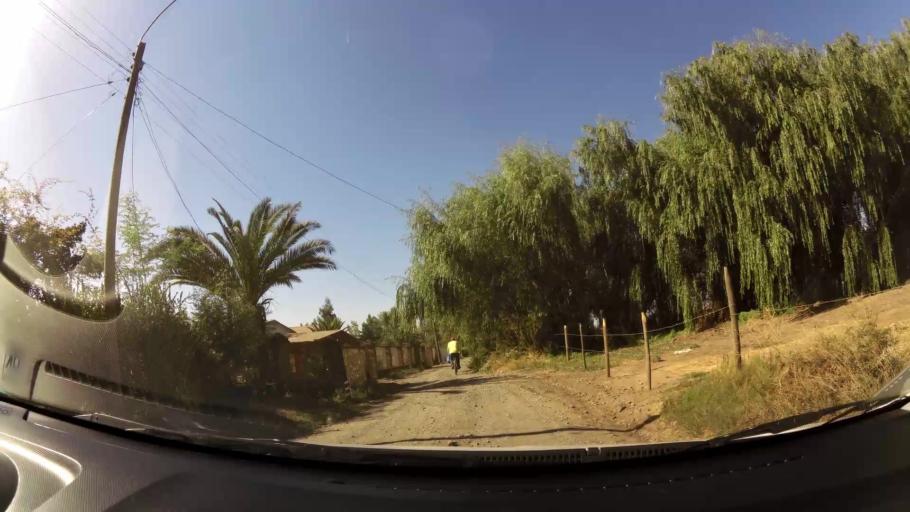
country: CL
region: Maule
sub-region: Provincia de Talca
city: Talca
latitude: -35.4194
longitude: -71.6034
